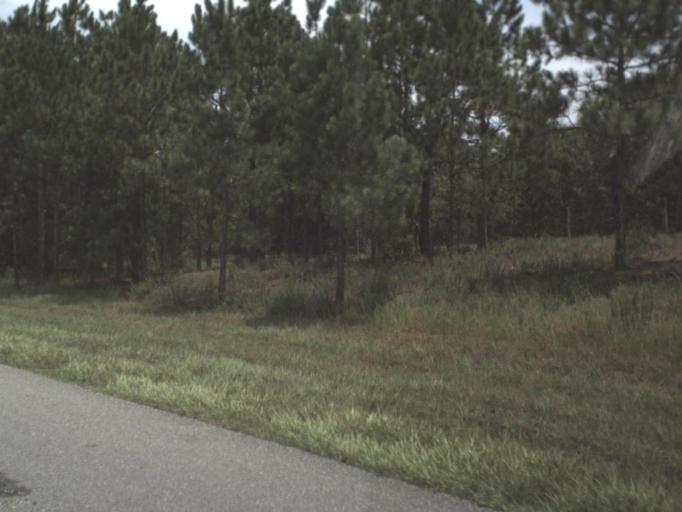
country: US
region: Florida
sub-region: Hernando County
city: Hill 'n Dale
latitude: 28.5453
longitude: -82.2369
